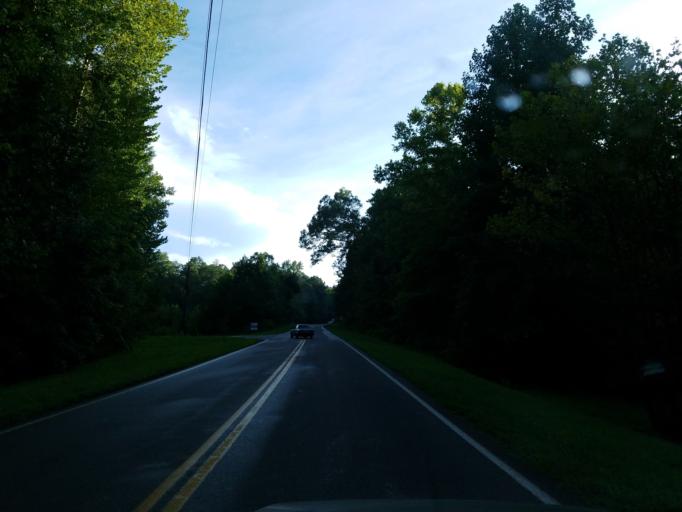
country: US
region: Georgia
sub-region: Lumpkin County
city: Dahlonega
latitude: 34.5418
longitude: -83.8892
